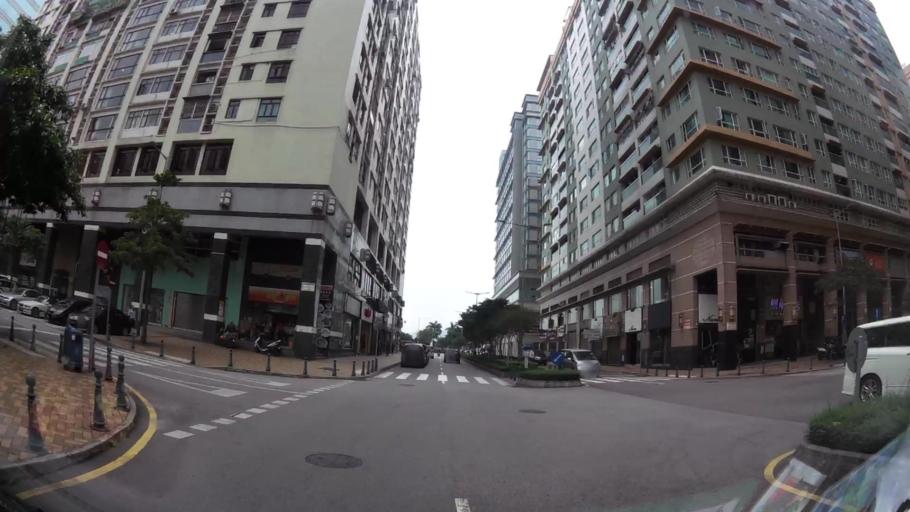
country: MO
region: Macau
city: Macau
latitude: 22.1887
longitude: 113.5529
